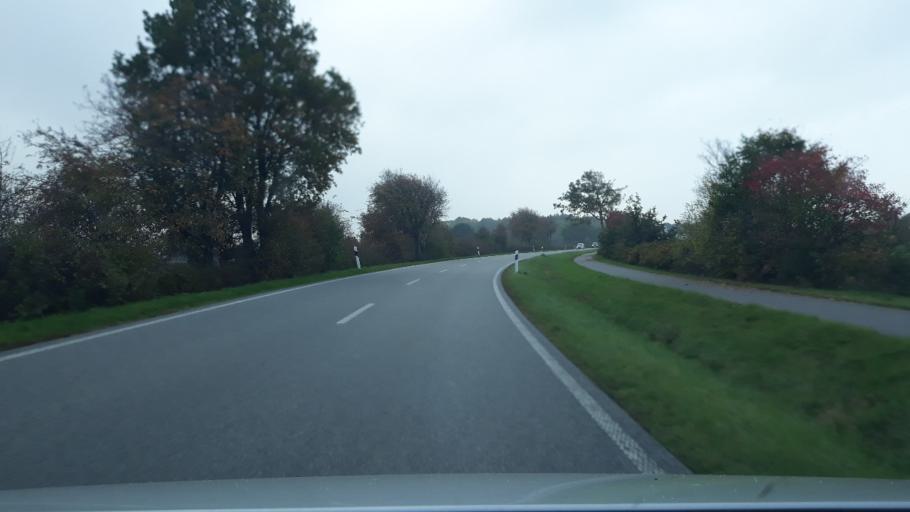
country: DE
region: Schleswig-Holstein
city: Dannewerk
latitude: 54.4699
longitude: 9.4927
